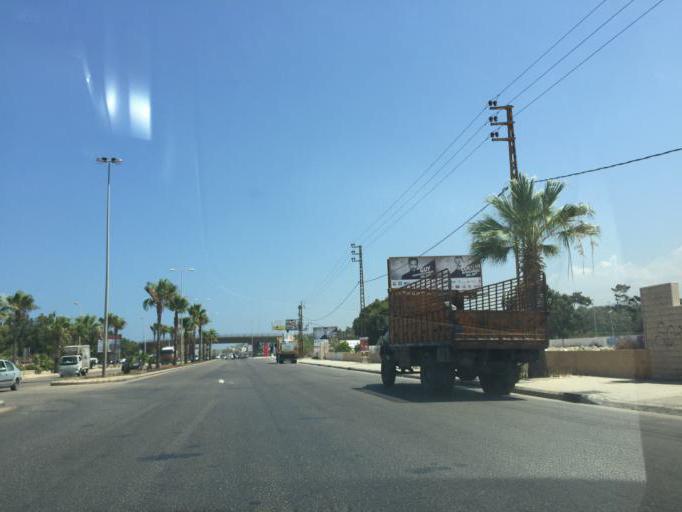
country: LB
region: Liban-Sud
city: Sidon
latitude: 33.5852
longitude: 35.3861
